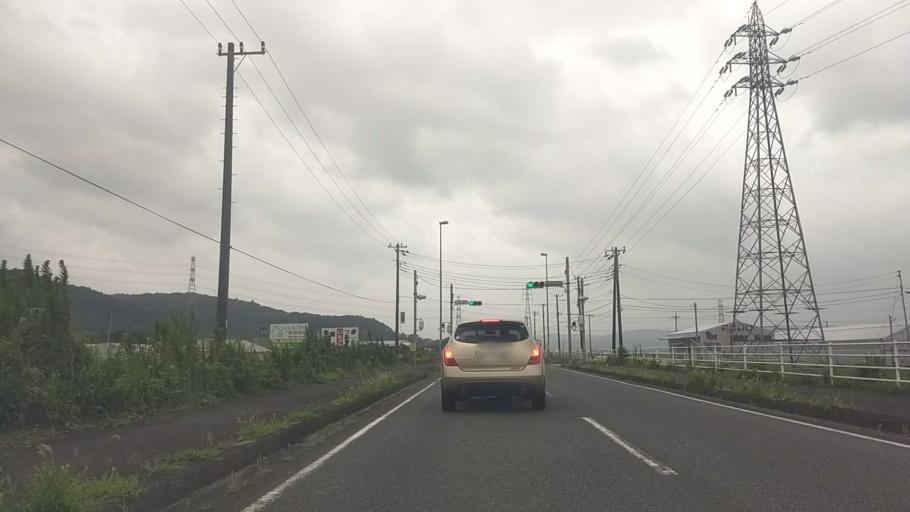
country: JP
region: Chiba
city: Kisarazu
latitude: 35.3511
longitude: 140.0548
